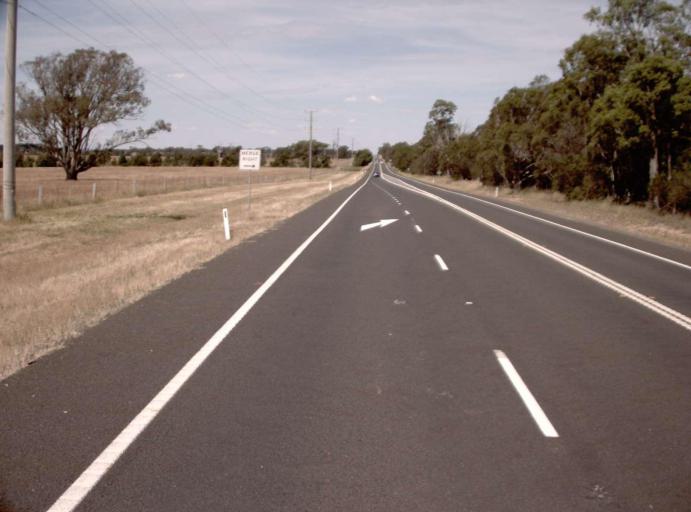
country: AU
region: Victoria
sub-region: East Gippsland
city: Bairnsdale
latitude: -37.8837
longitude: 147.4102
